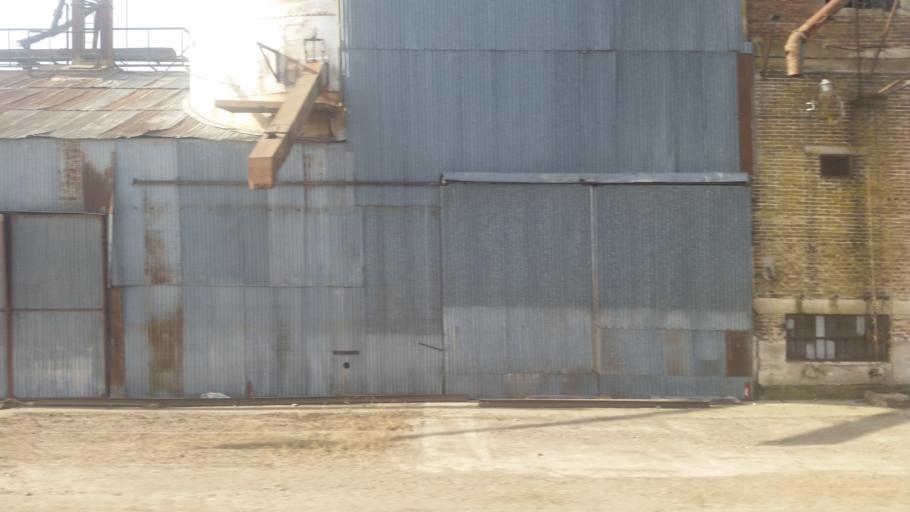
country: AR
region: Cordoba
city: Laguna Larga
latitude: -31.7800
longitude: -63.8002
